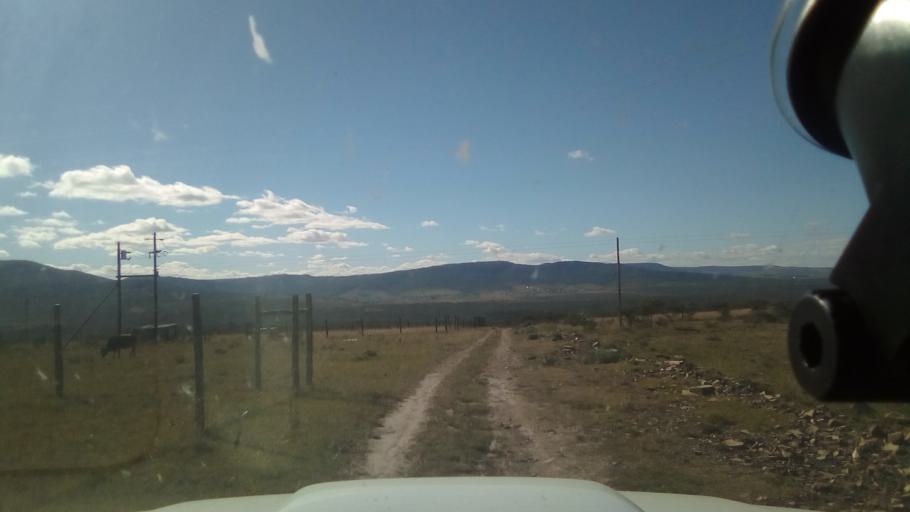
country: ZA
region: Eastern Cape
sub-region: Buffalo City Metropolitan Municipality
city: Bhisho
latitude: -32.7795
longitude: 27.3357
